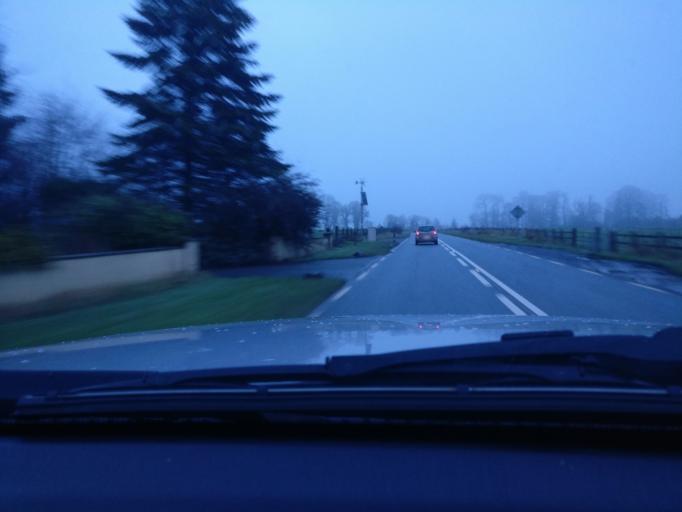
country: IE
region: Leinster
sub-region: An Mhi
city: Athboy
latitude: 53.6441
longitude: -6.8761
